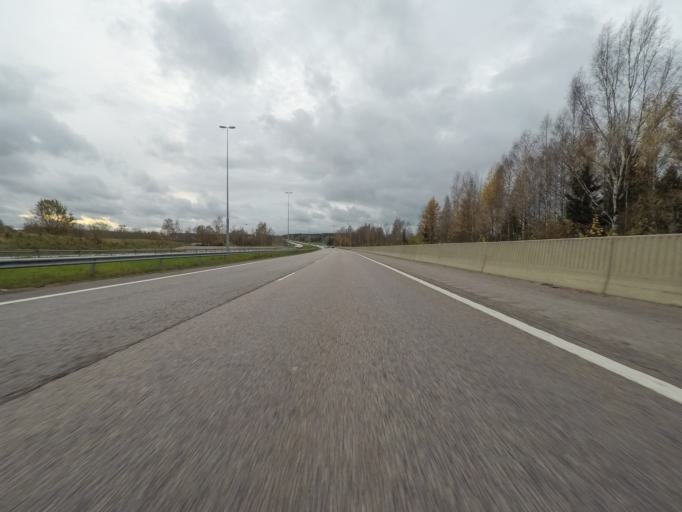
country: FI
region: Uusimaa
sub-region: Porvoo
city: Porvoo
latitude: 60.4125
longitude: 25.6452
